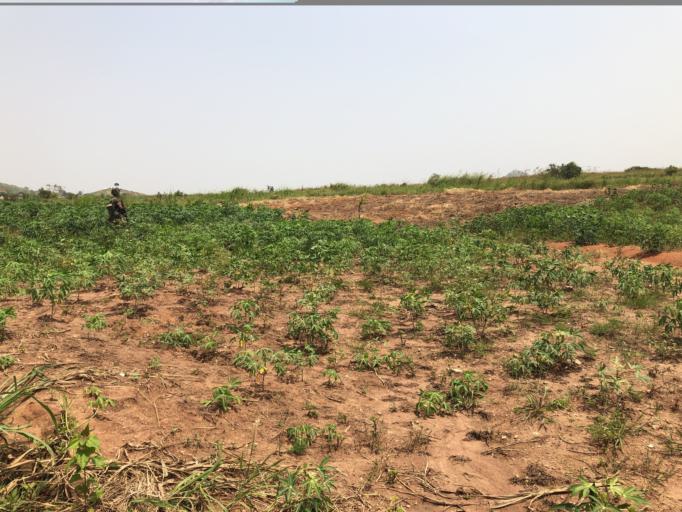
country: CD
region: Nord Kivu
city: Beni
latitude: 0.4654
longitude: 29.5287
